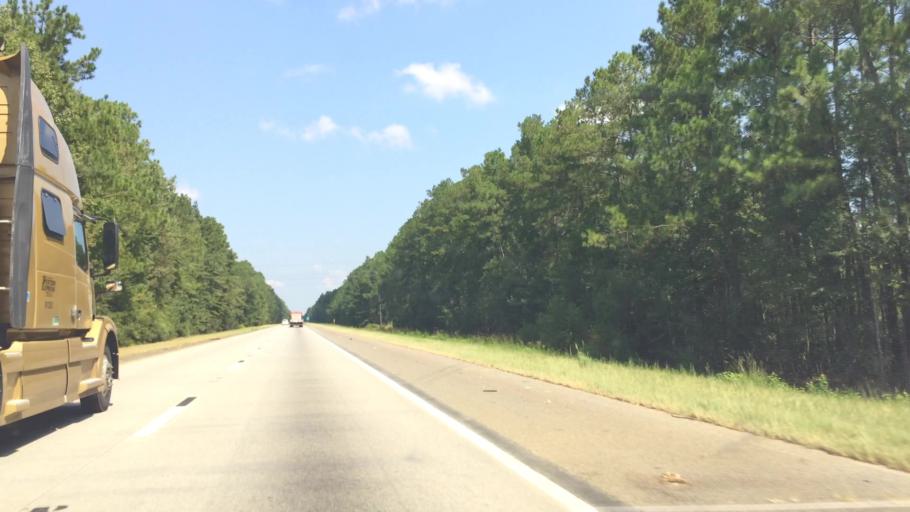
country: US
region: South Carolina
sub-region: Colleton County
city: Walterboro
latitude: 33.0580
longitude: -80.6643
